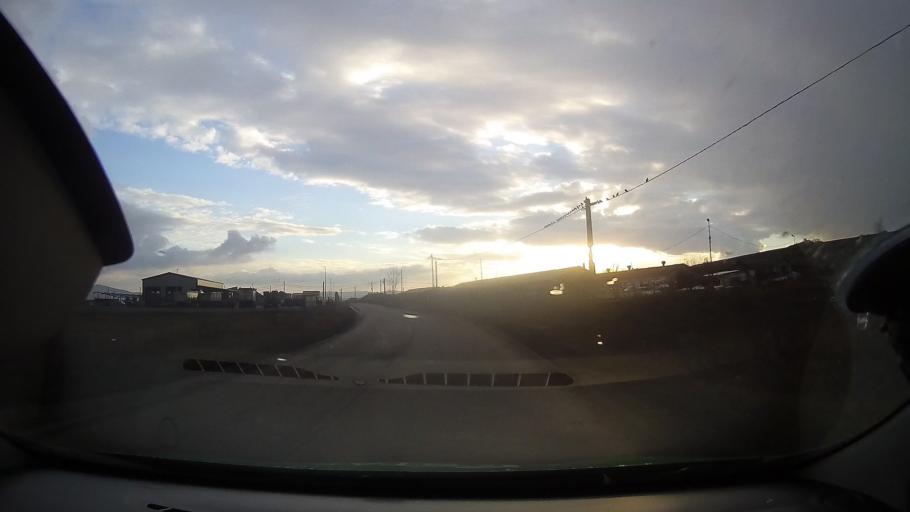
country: RO
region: Alba
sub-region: Comuna Lunca Muresului
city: Lunca Muresului
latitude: 46.4410
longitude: 23.9099
